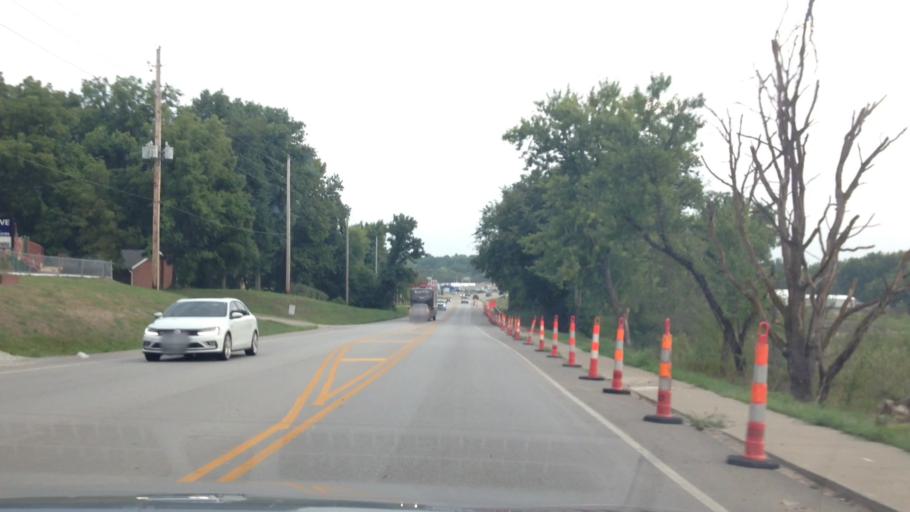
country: US
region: Missouri
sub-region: Clay County
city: Smithville
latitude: 39.3975
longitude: -94.5836
